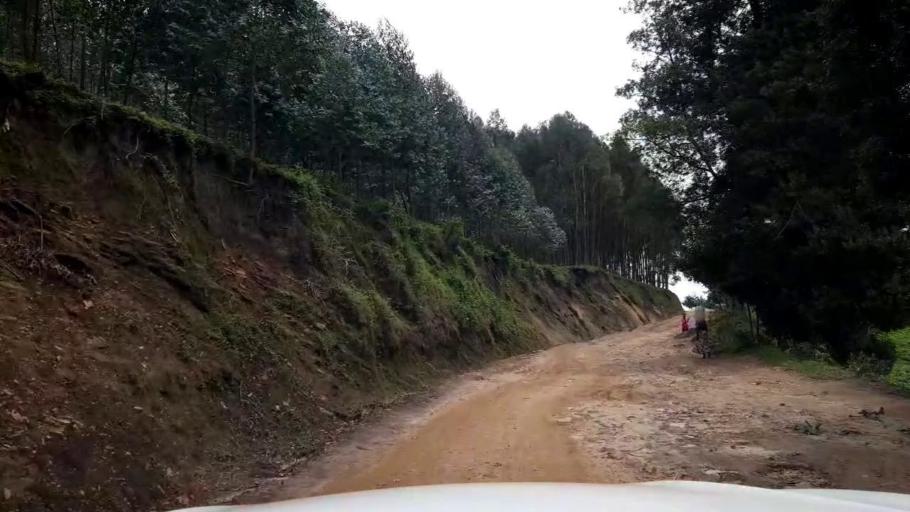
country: RW
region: Western Province
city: Kibuye
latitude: -1.9514
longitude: 29.4099
